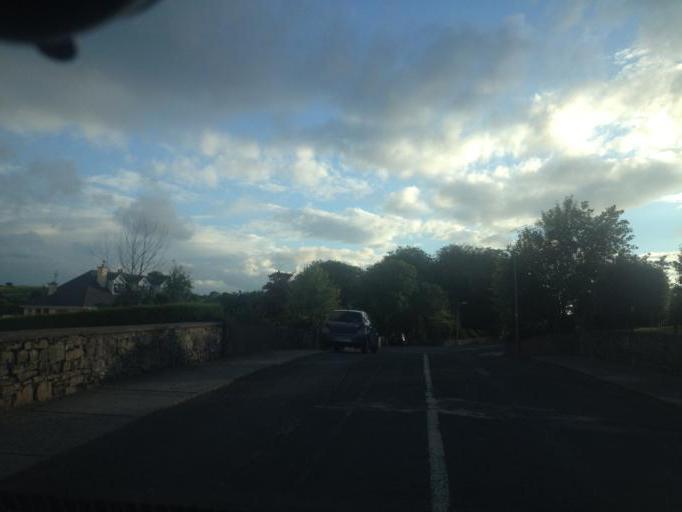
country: IE
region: Connaught
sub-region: Sligo
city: Sligo
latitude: 54.2834
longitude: -8.3966
